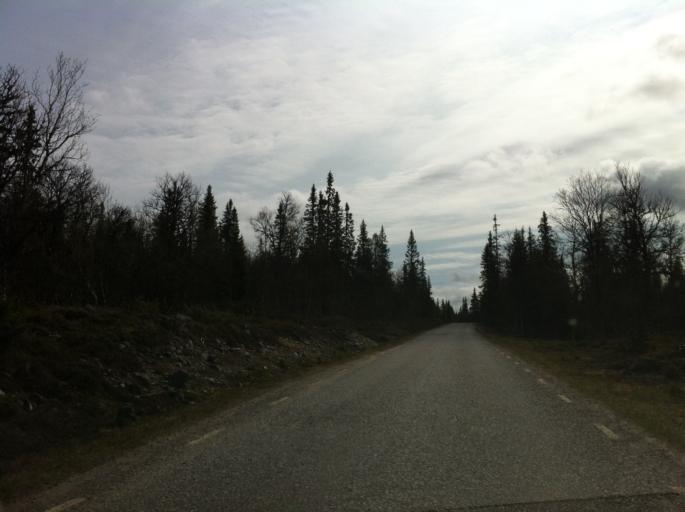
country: NO
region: Hedmark
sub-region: Engerdal
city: Engerdal
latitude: 62.3061
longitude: 12.8043
